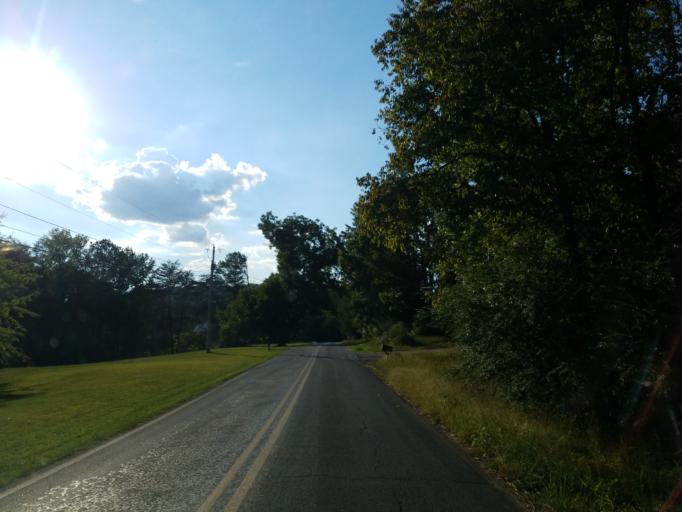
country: US
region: Georgia
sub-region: Murray County
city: Chatsworth
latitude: 34.9495
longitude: -84.7325
